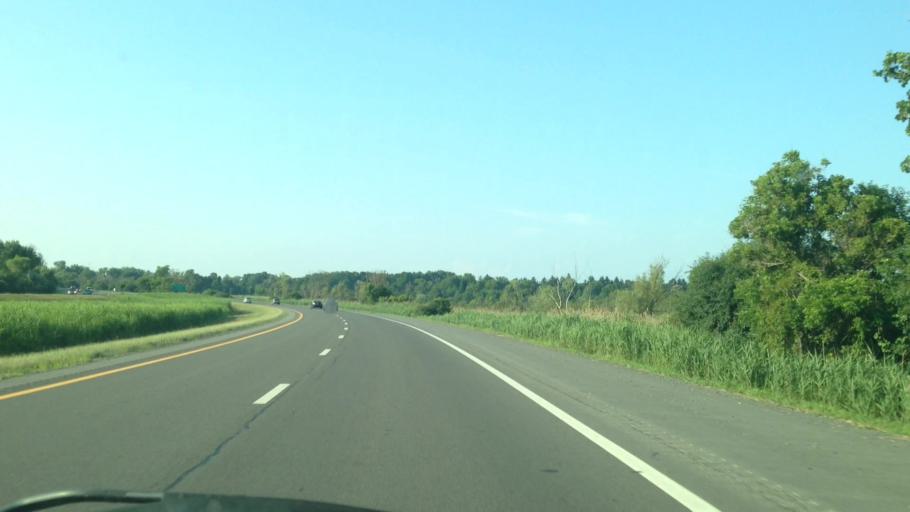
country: US
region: New York
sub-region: Onondaga County
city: East Syracuse
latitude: 43.0195
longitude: -76.0631
